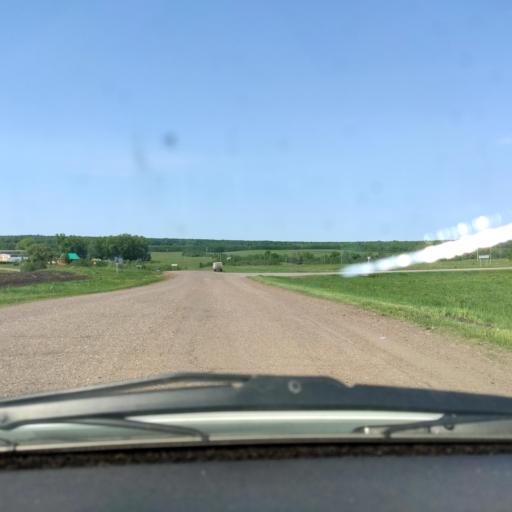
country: RU
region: Bashkortostan
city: Chishmy
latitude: 54.4731
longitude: 55.5414
